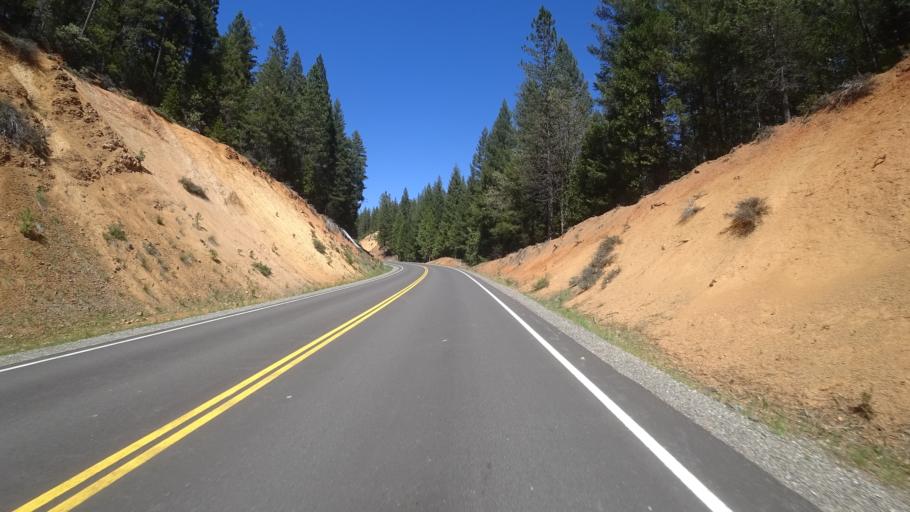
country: US
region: California
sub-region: Trinity County
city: Lewiston
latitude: 40.8932
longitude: -122.7936
